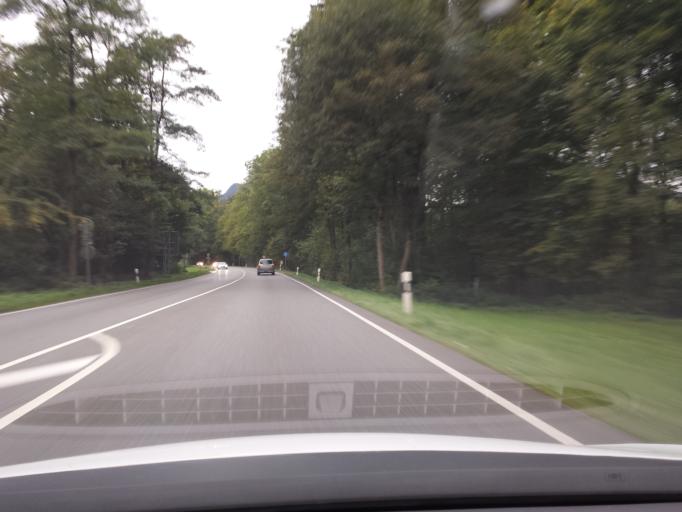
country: DE
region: Bavaria
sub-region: Upper Bavaria
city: Bad Reichenhall
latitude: 47.7309
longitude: 12.8705
